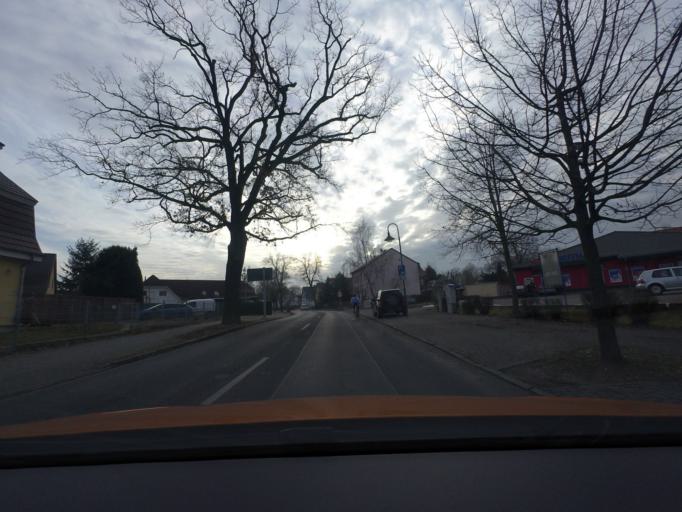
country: DE
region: Berlin
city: Blankenfelde
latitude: 52.6618
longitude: 13.3777
